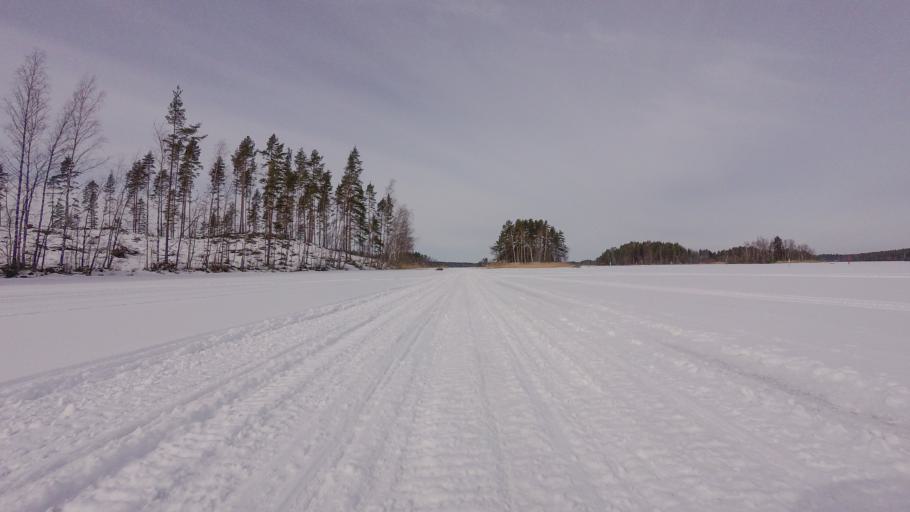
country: FI
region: Southern Savonia
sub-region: Savonlinna
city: Heinaevesi
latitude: 62.1224
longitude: 28.6174
